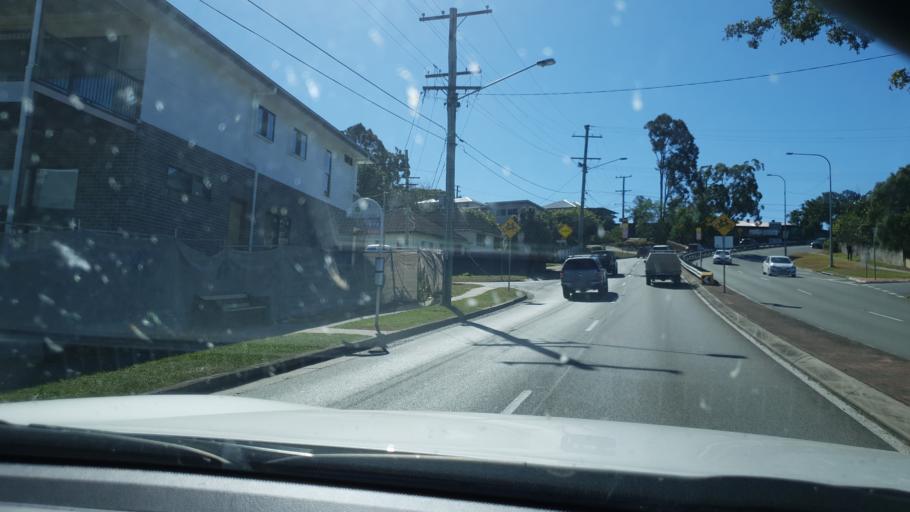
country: AU
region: Queensland
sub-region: Brisbane
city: Everton Park
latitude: -27.3999
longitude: 152.9863
